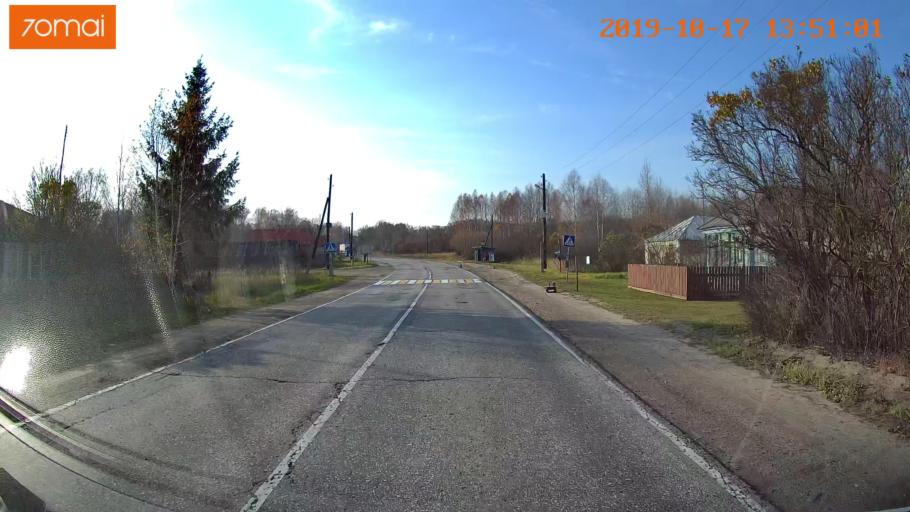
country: RU
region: Rjazan
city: Tuma
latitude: 55.1400
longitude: 40.3962
